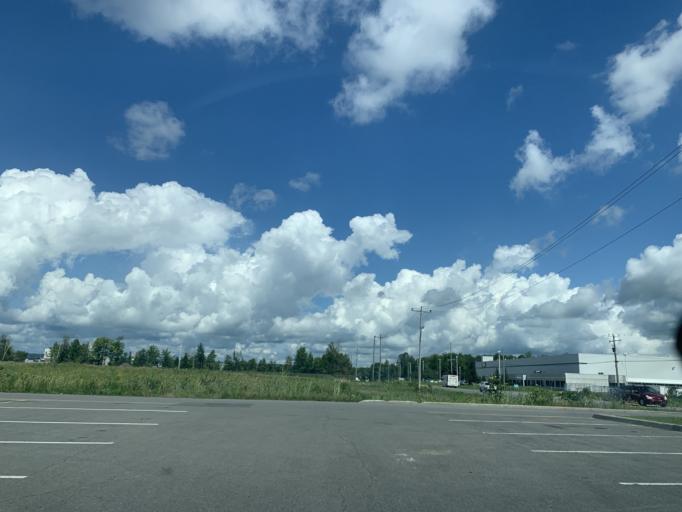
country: CA
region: Ontario
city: Hawkesbury
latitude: 45.5907
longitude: -74.5915
